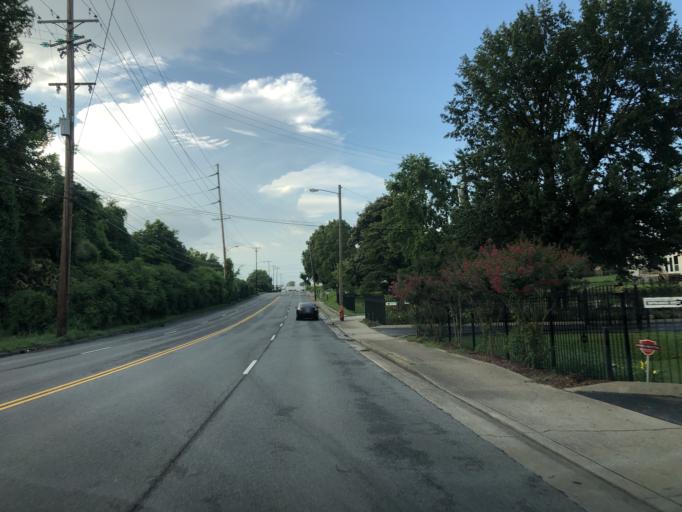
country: US
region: Tennessee
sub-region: Davidson County
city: Nashville
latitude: 36.1492
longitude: -86.7220
